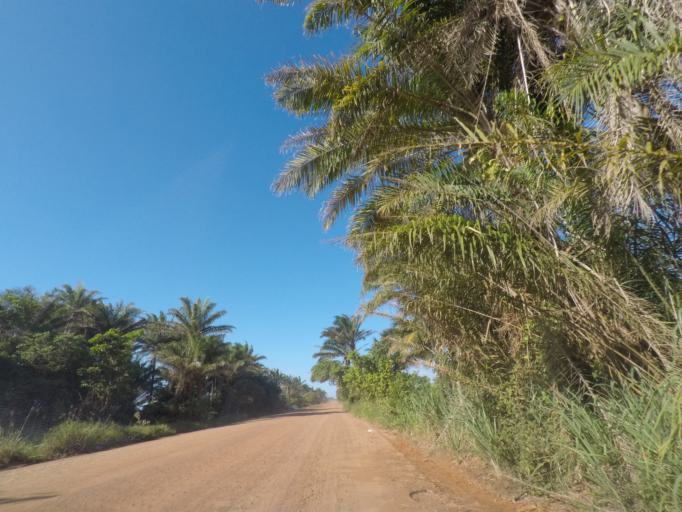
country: BR
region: Bahia
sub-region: Marau
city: Marau
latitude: -14.0610
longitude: -38.9575
